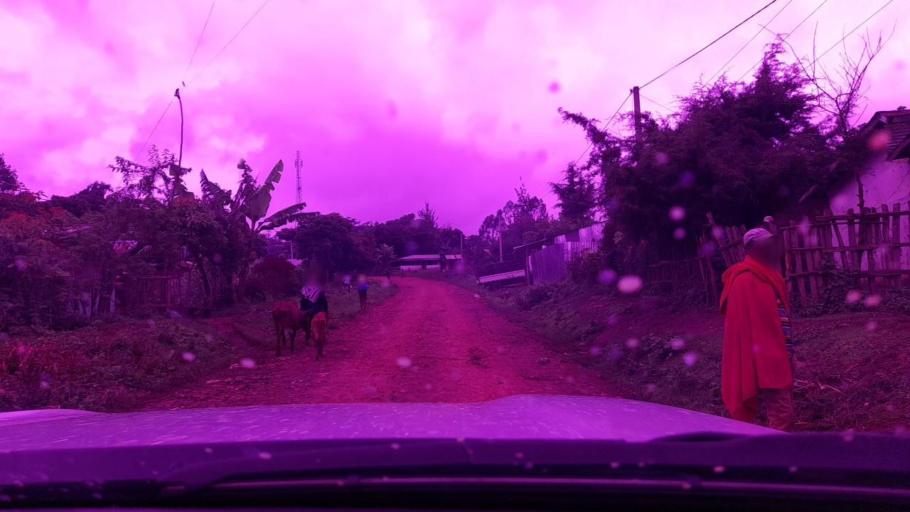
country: ET
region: Southern Nations, Nationalities, and People's Region
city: Bonga
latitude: 7.5529
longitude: 35.8603
